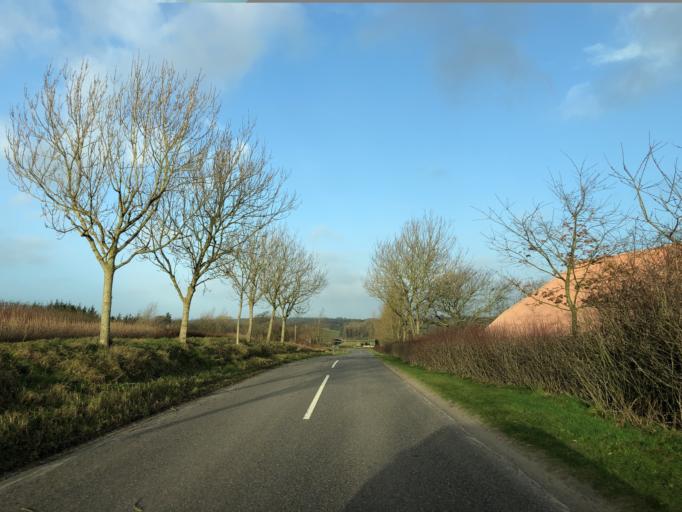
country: DK
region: Central Jutland
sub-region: Ringkobing-Skjern Kommune
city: Videbaek
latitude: 56.1923
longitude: 8.5421
